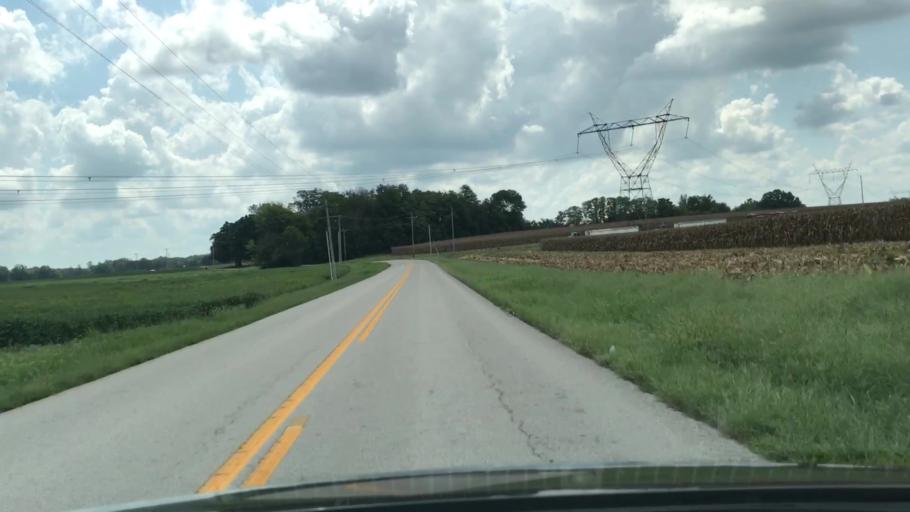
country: US
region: Kentucky
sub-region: Todd County
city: Elkton
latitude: 36.7734
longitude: -87.1178
